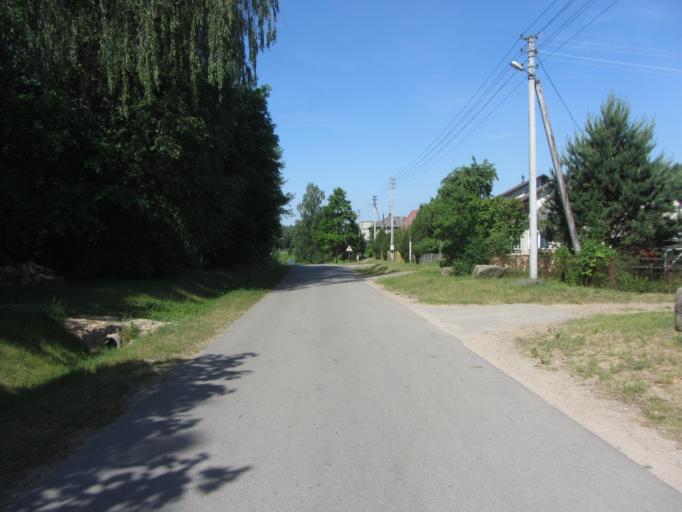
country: LT
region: Kauno apskritis
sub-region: Kauno rajonas
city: Karmelava
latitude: 54.8960
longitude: 24.1534
